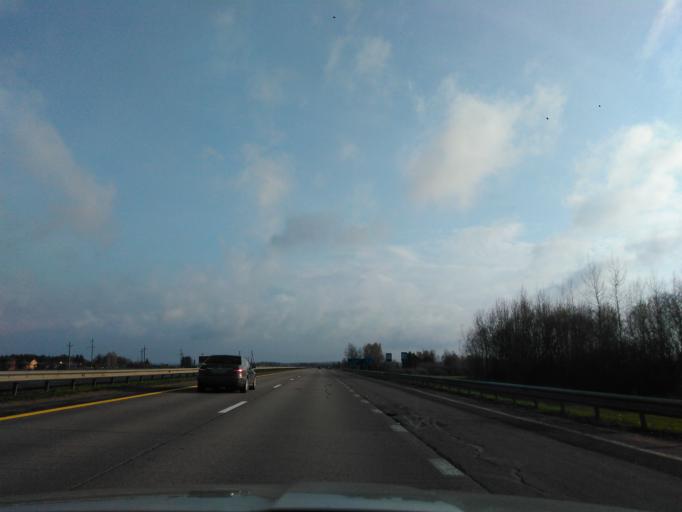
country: BY
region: Minsk
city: Lahoysk
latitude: 54.1635
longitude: 27.8157
